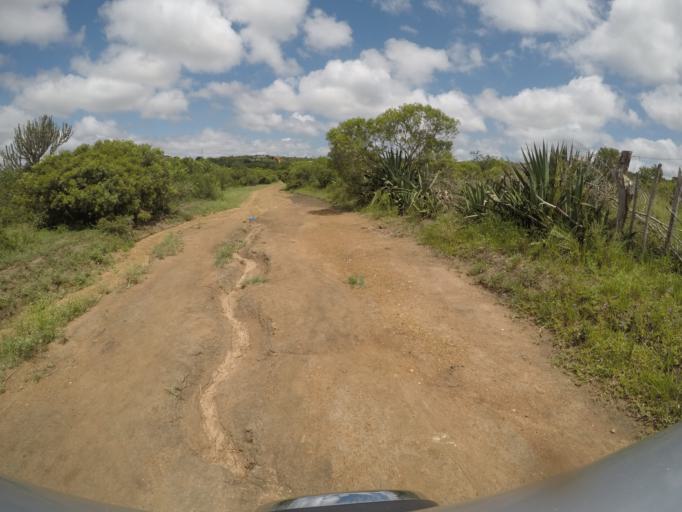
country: ZA
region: KwaZulu-Natal
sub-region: uThungulu District Municipality
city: Empangeni
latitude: -28.5795
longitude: 31.8373
